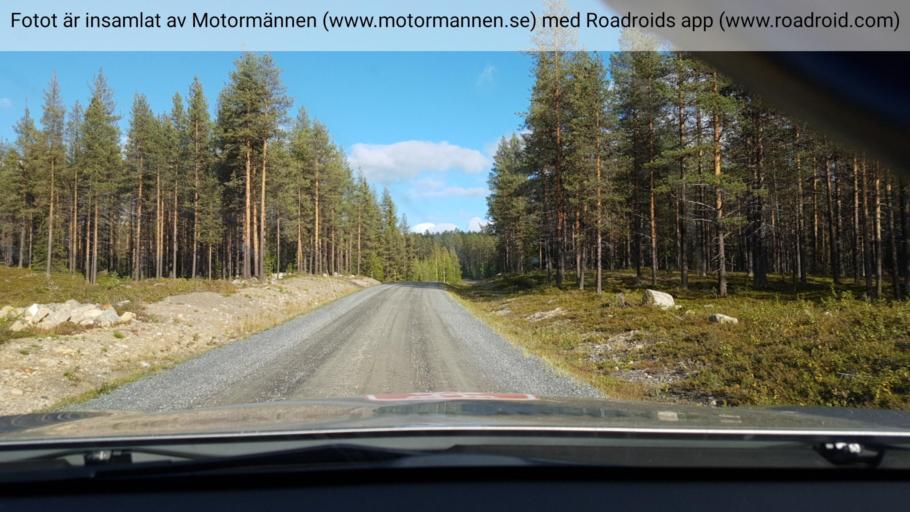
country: SE
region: Vaesterbotten
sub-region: Sorsele Kommun
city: Sorsele
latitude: 65.4501
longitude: 18.1226
